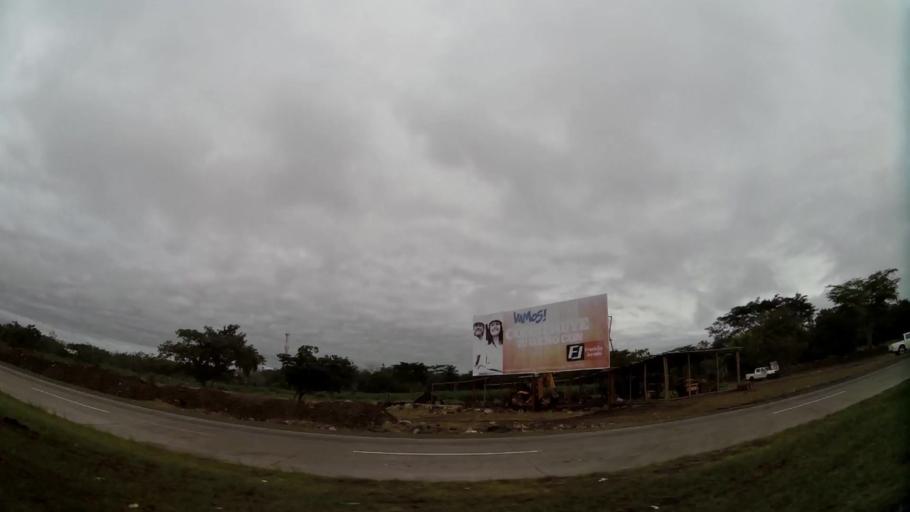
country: PA
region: Chiriqui
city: Bugaba
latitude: 8.4997
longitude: -82.5986
